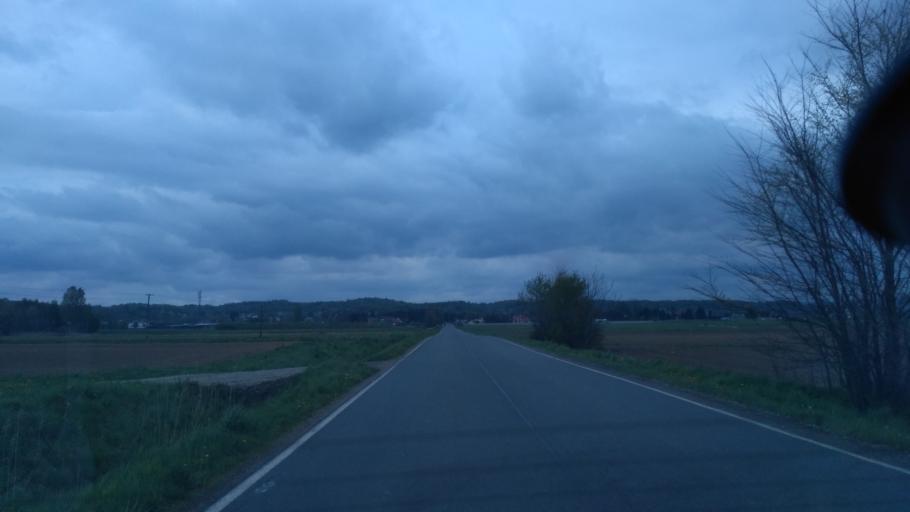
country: PL
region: Subcarpathian Voivodeship
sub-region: Powiat brzozowski
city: Jasionow
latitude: 49.6538
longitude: 21.9855
